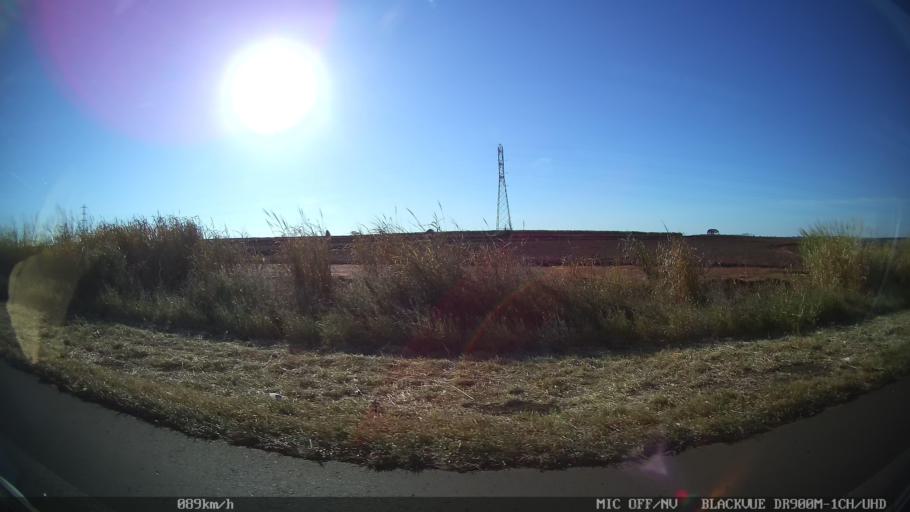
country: BR
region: Sao Paulo
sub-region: Olimpia
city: Olimpia
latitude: -20.6983
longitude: -48.9338
